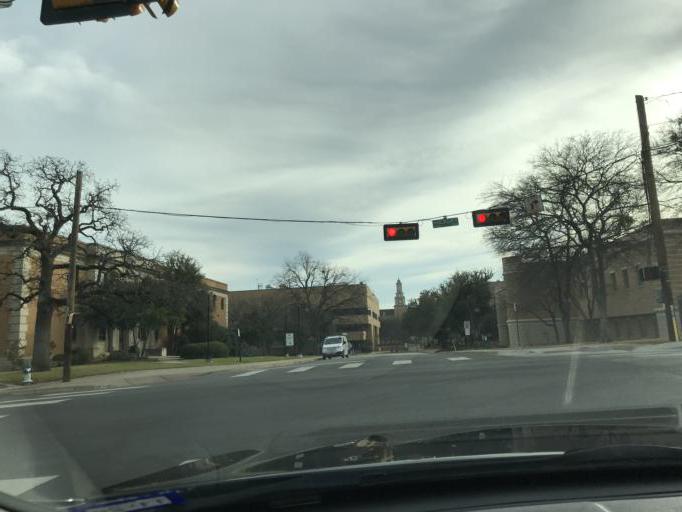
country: US
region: Texas
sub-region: Denton County
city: Denton
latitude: 33.2148
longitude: -97.1484
